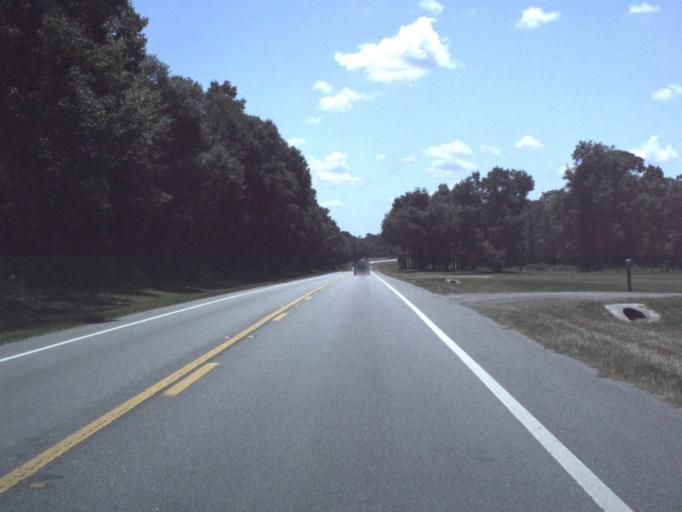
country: US
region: Florida
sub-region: Suwannee County
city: Wellborn
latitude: 30.3174
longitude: -82.7220
